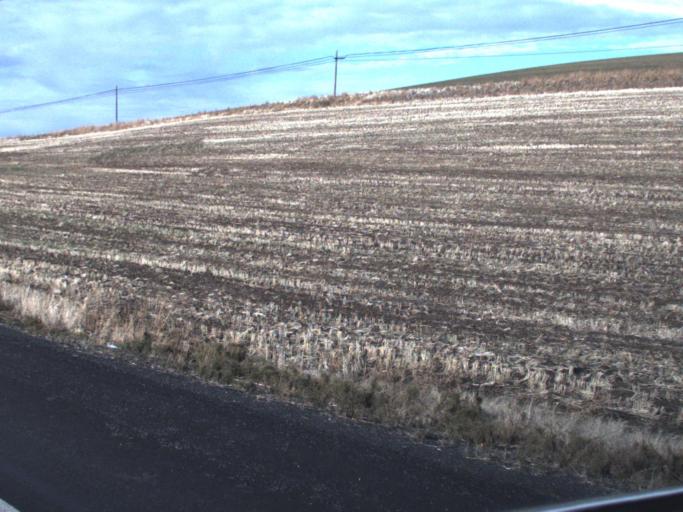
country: US
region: Washington
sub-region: Whitman County
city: Pullman
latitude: 46.7343
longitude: -117.2172
